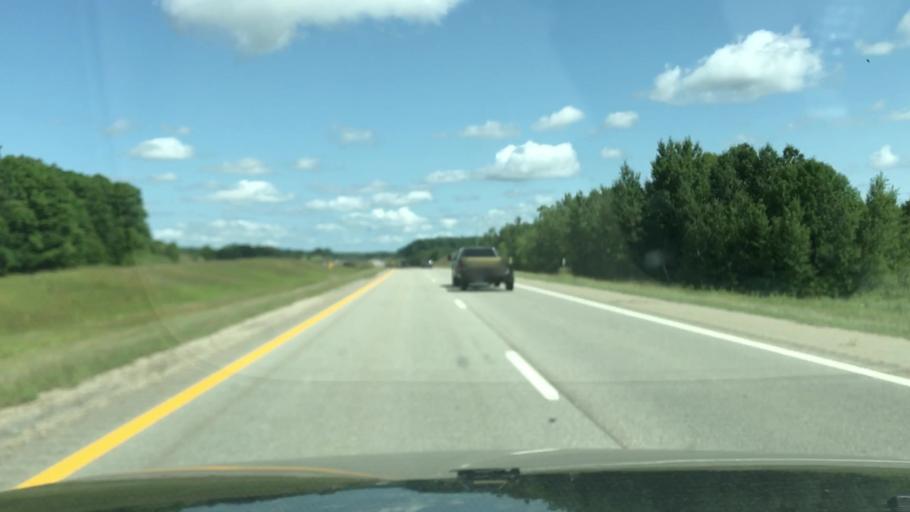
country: US
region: Michigan
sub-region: Mecosta County
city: Big Rapids
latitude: 43.7773
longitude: -85.5340
